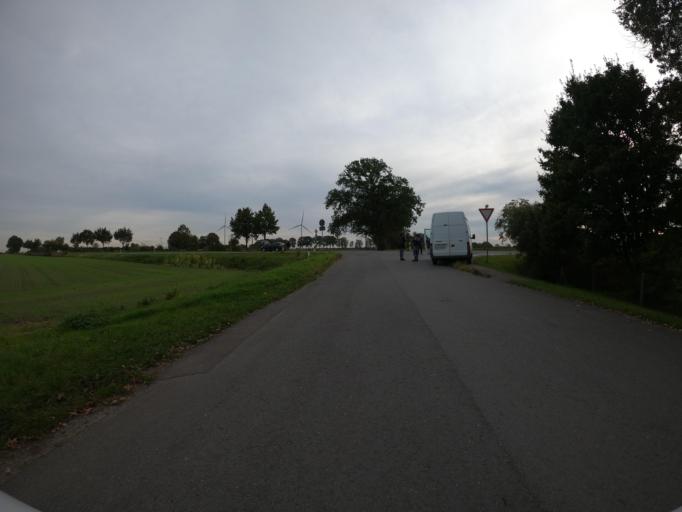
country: DE
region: North Rhine-Westphalia
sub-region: Regierungsbezirk Dusseldorf
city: Schermbeck
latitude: 51.6898
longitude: 6.9010
